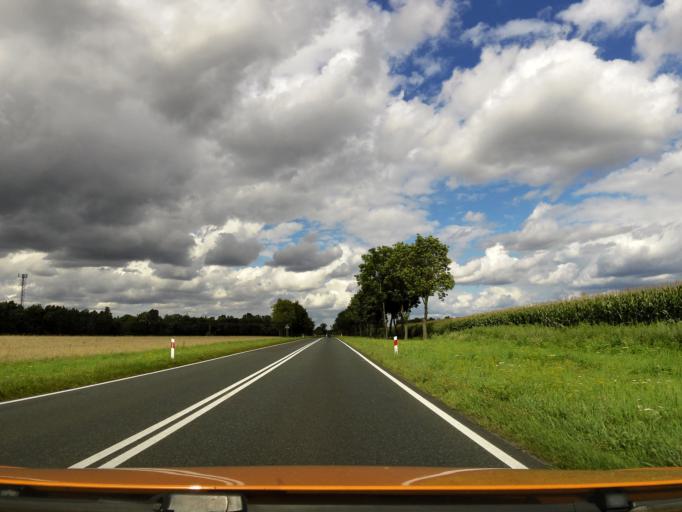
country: PL
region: West Pomeranian Voivodeship
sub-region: Powiat gryficki
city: Ploty
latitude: 53.7416
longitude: 15.2117
